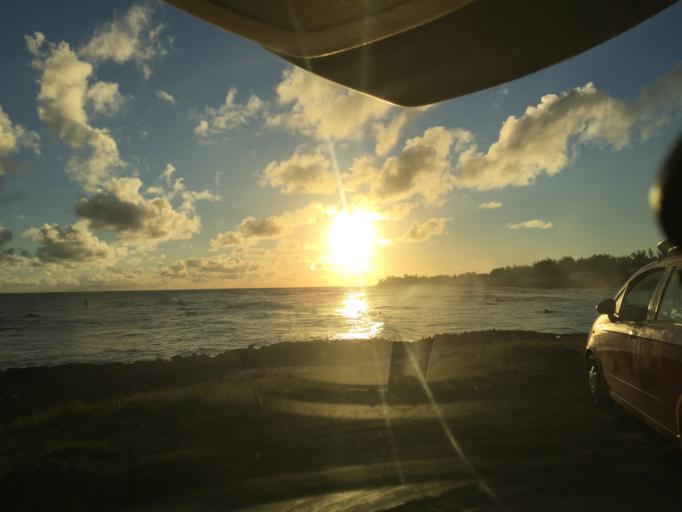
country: BB
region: Christ Church
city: Oistins
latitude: 13.0522
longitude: -59.5045
